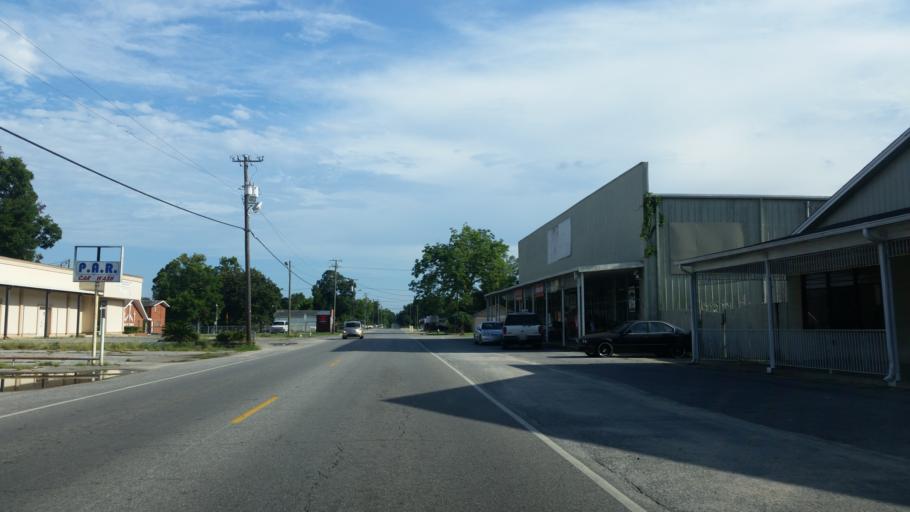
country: US
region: Florida
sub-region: Escambia County
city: Goulding
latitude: 30.4323
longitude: -87.2462
